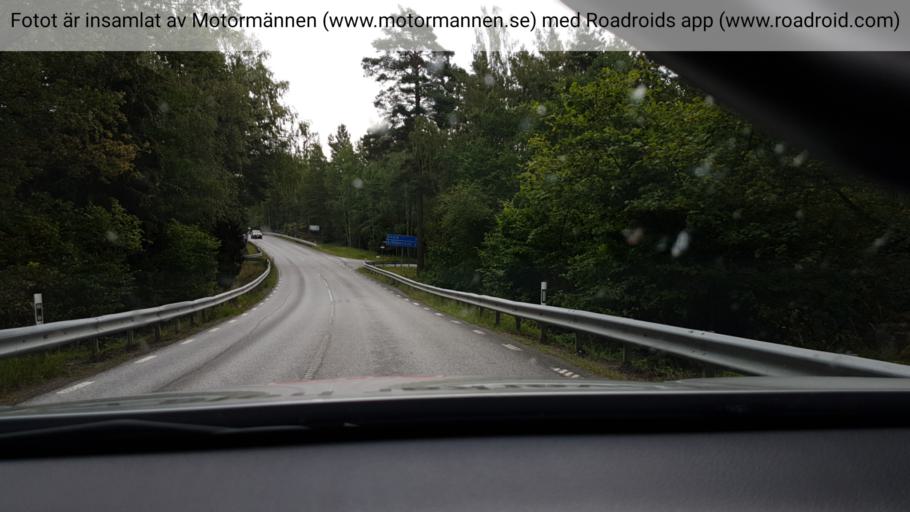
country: SE
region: Stockholm
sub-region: Vaxholms Kommun
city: Resaro
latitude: 59.5466
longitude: 18.5167
